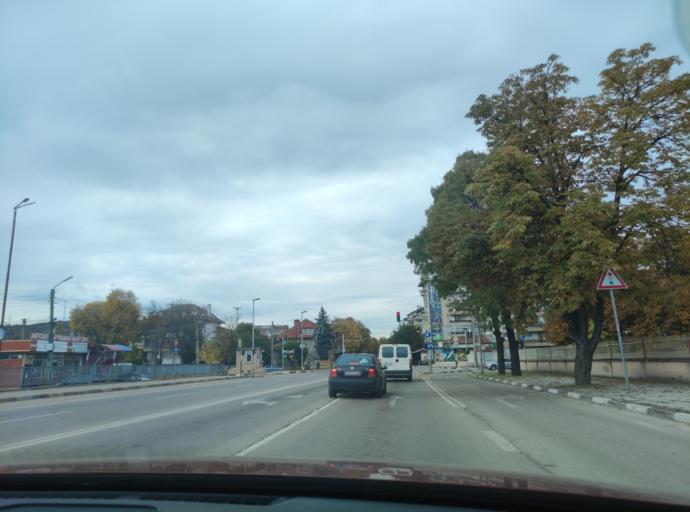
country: BG
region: Montana
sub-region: Obshtina Montana
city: Montana
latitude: 43.4028
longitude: 23.2293
